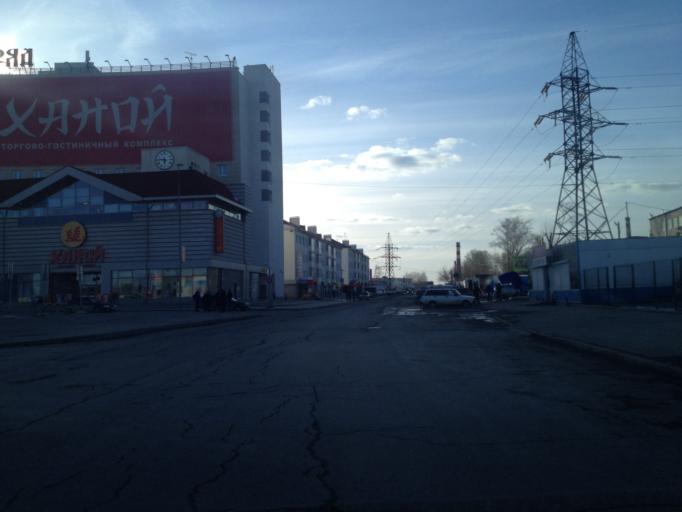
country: RU
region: Sverdlovsk
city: Yekaterinburg
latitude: 56.8616
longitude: 60.5386
